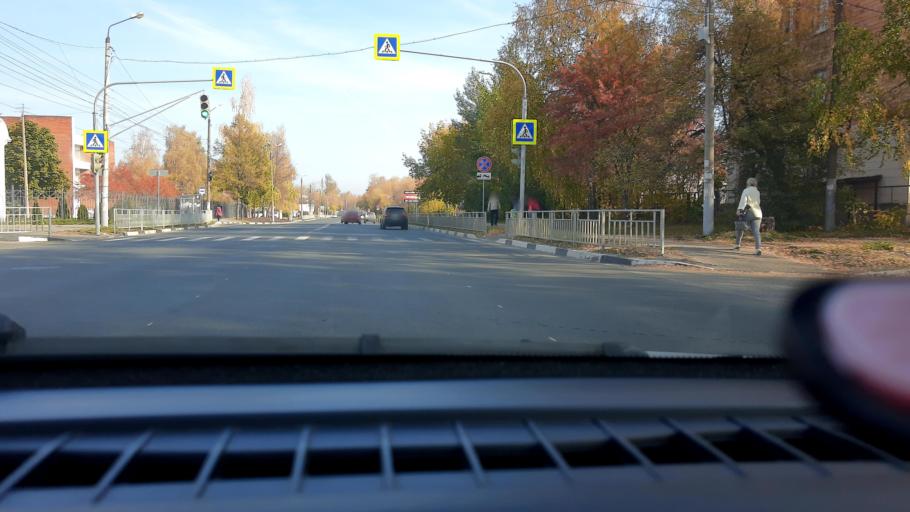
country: RU
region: Nizjnij Novgorod
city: Kstovo
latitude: 56.1511
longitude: 44.1874
